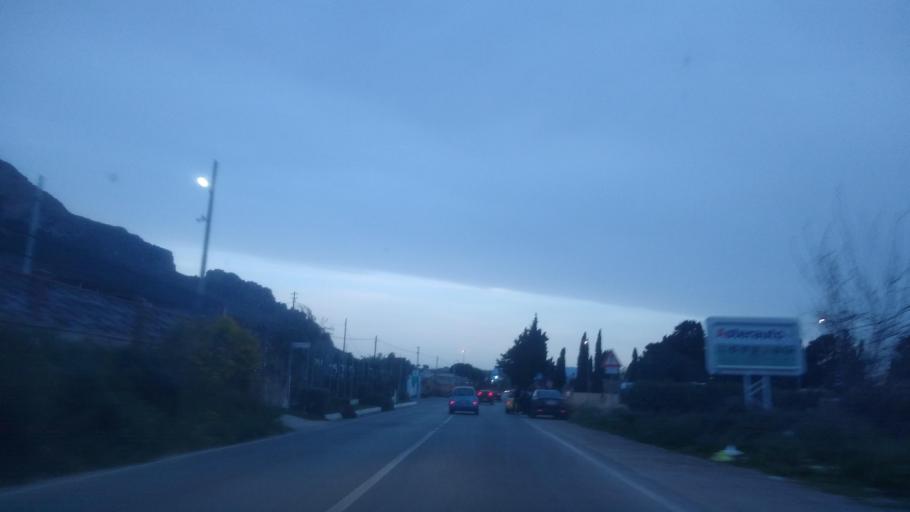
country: IT
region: Sicily
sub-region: Palermo
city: Terrasini
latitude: 38.1431
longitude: 13.0858
